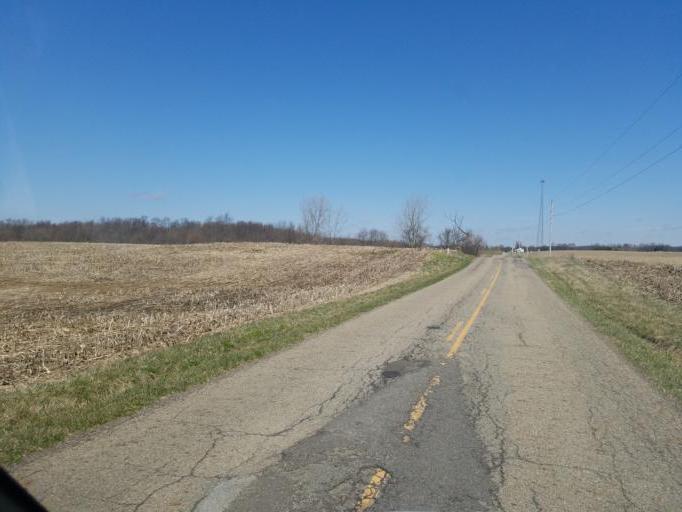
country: US
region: Ohio
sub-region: Knox County
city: Centerburg
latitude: 40.3364
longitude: -82.7266
